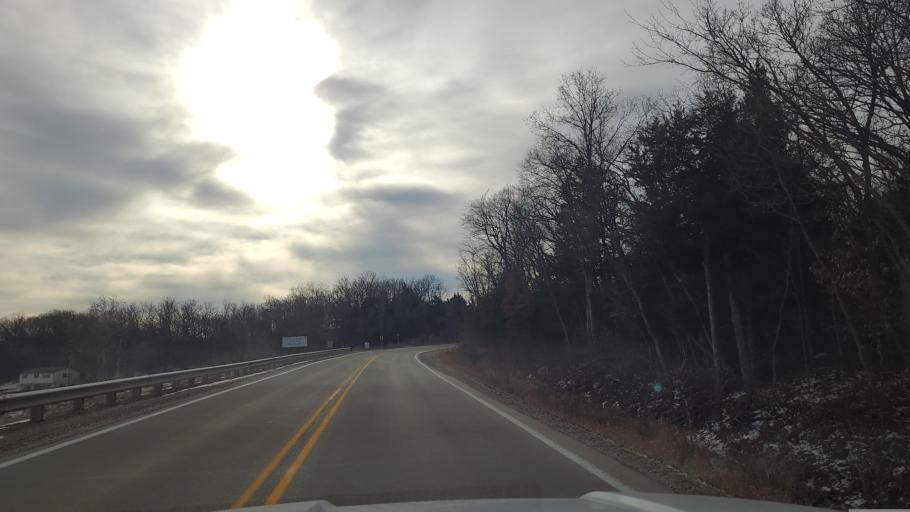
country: US
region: Kansas
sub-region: Douglas County
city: Baldwin City
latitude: 38.8078
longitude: -95.1858
